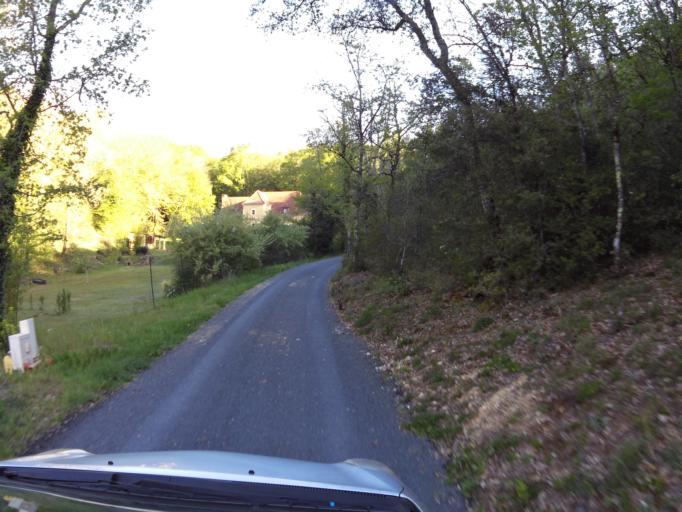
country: FR
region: Aquitaine
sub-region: Departement de la Dordogne
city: Carsac-Aillac
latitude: 44.8206
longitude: 1.2995
